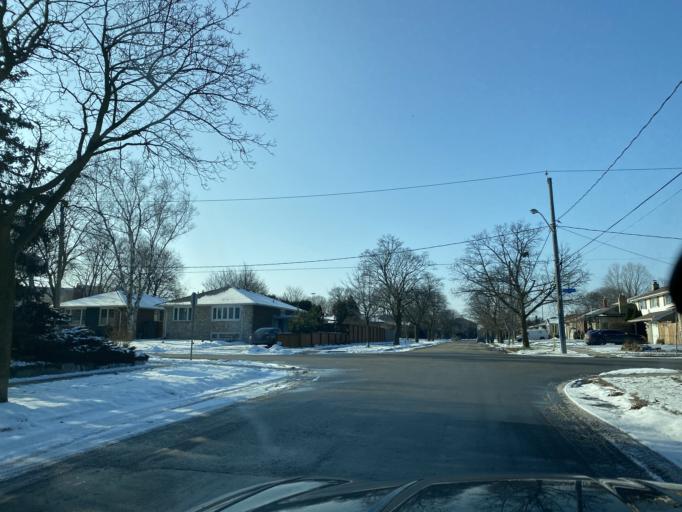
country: CA
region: Ontario
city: Etobicoke
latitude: 43.6617
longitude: -79.5665
